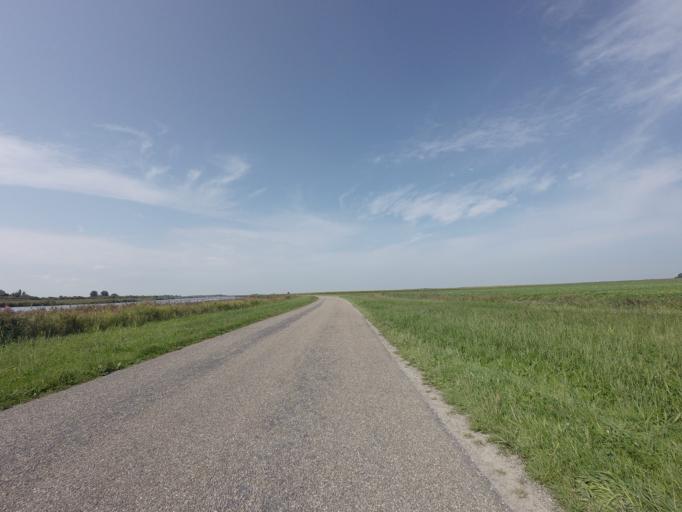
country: NL
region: Groningen
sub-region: Gemeente De Marne
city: Ulrum
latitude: 53.3411
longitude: 6.2903
